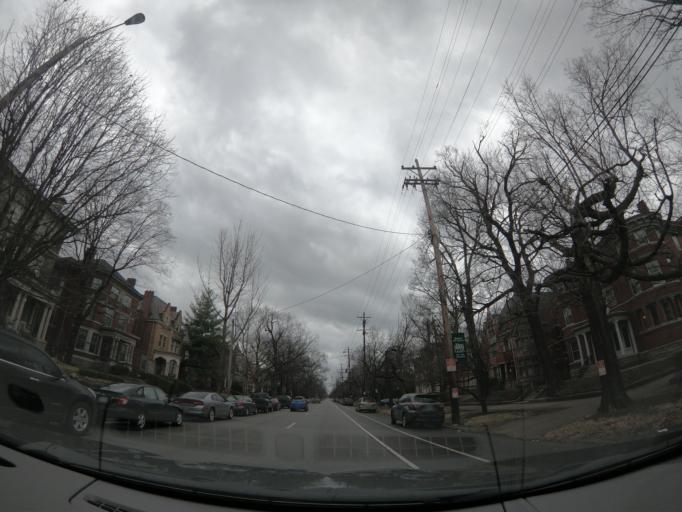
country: US
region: Kentucky
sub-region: Jefferson County
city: Louisville
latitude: 38.2317
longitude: -85.7592
